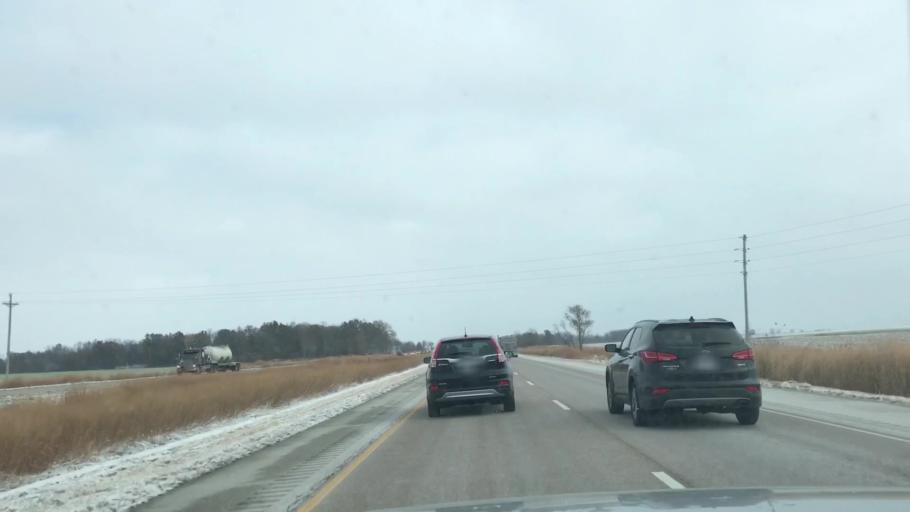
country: US
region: Illinois
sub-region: Macoupin County
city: Mount Olive
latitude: 39.1242
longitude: -89.7171
